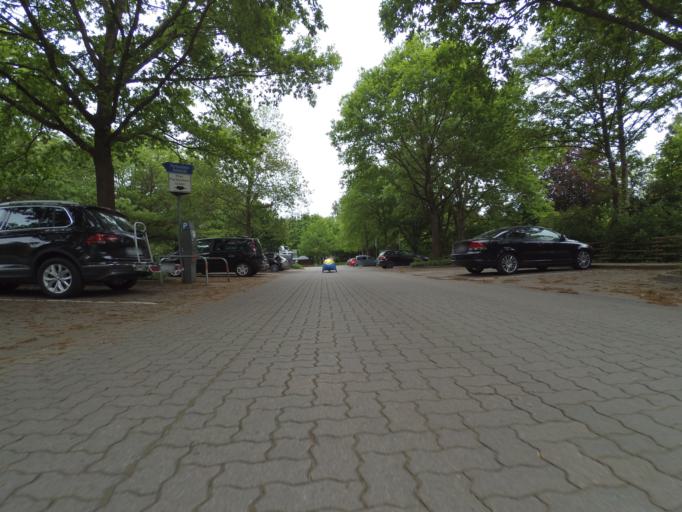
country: DE
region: Lower Saxony
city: Hagenburg
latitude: 52.4513
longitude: 9.3523
